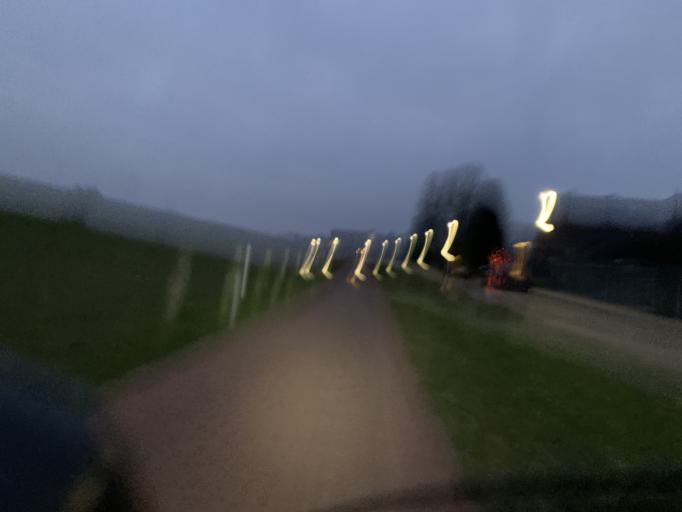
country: DE
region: North Rhine-Westphalia
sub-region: Regierungsbezirk Dusseldorf
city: Meerbusch
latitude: 51.2939
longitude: 6.7143
